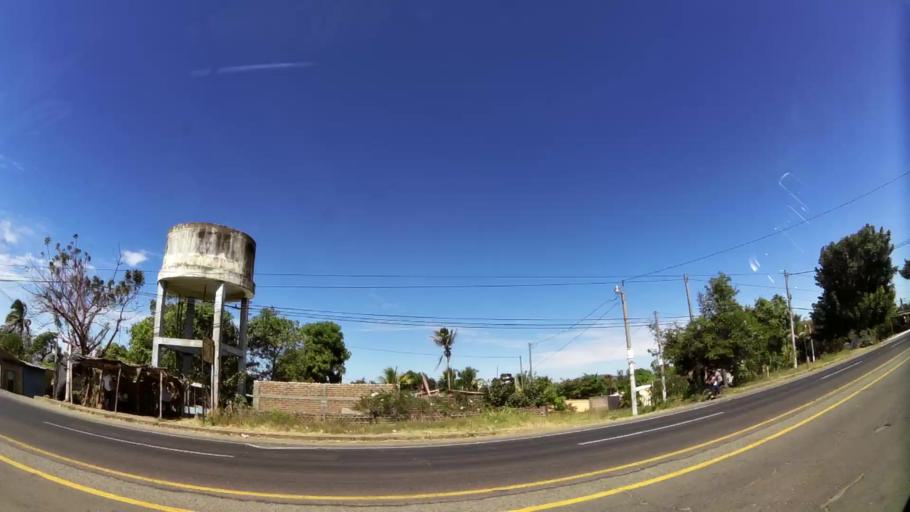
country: SV
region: Santa Ana
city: Chalchuapa
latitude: 13.9729
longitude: -89.7069
